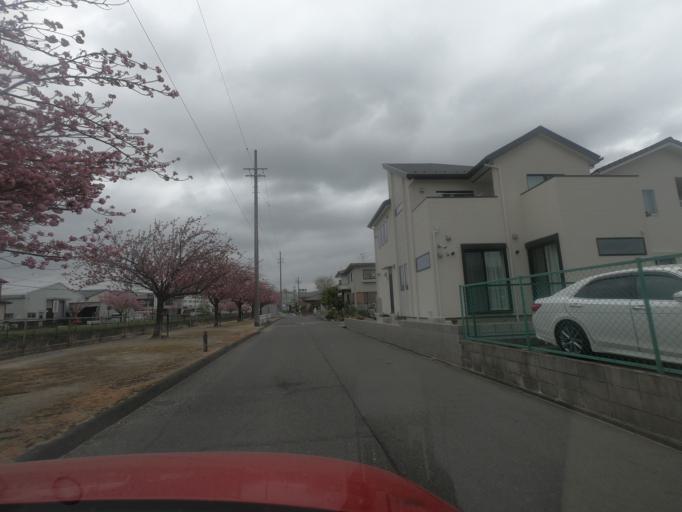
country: JP
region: Aichi
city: Kasugai
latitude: 35.2663
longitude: 136.9545
